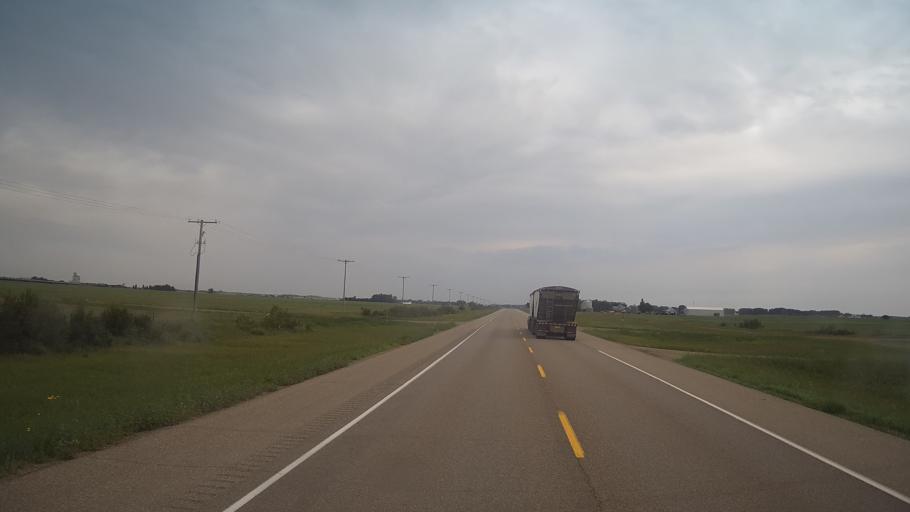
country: CA
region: Saskatchewan
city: Langham
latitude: 52.1288
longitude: -107.1922
